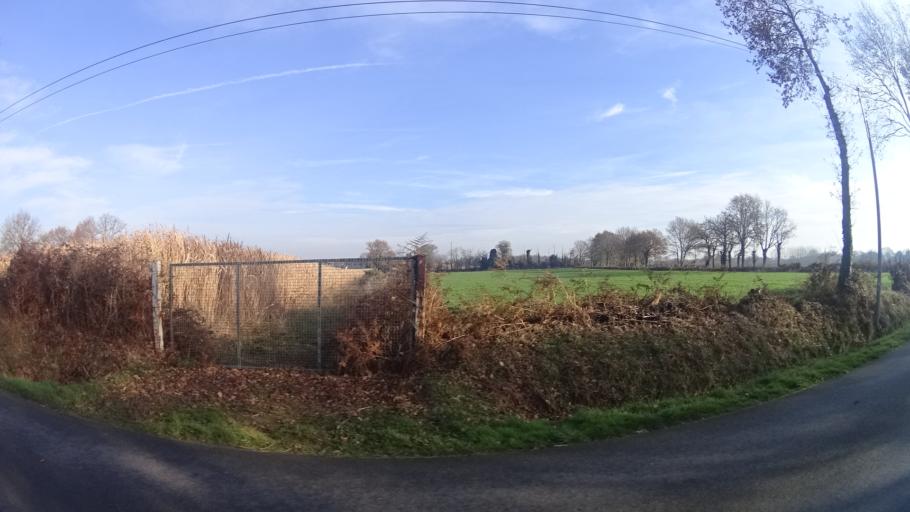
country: FR
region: Brittany
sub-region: Departement du Morbihan
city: Allaire
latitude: 47.6250
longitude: -2.1585
